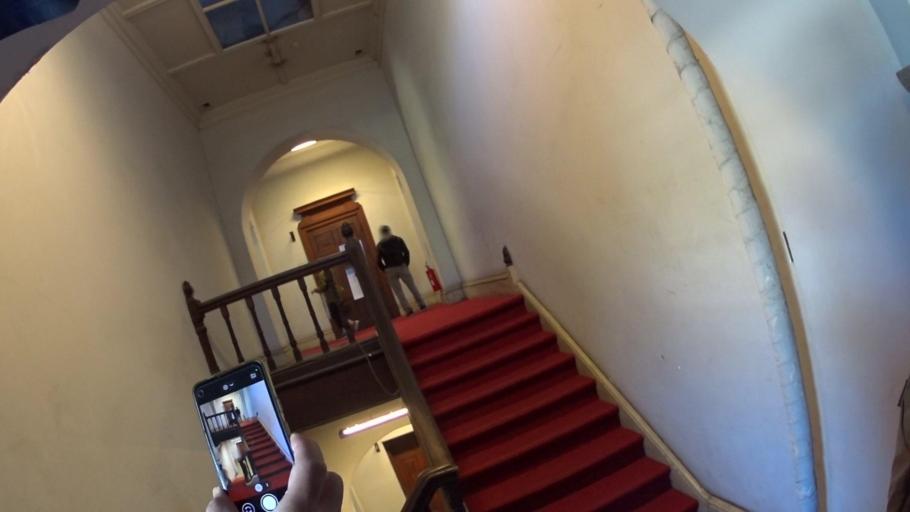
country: JP
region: Kyoto
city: Kyoto
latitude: 35.0207
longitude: 135.7561
